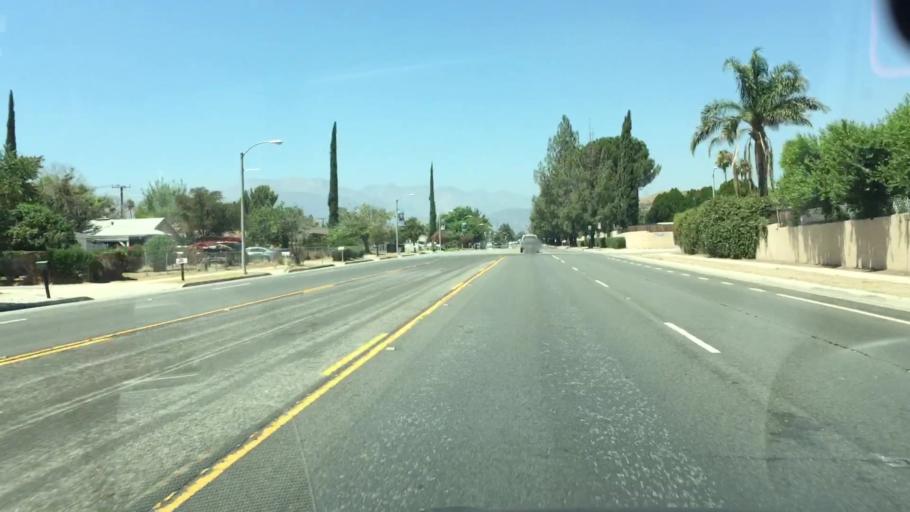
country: US
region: California
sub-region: San Bernardino County
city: Muscoy
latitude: 34.1725
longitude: -117.3231
